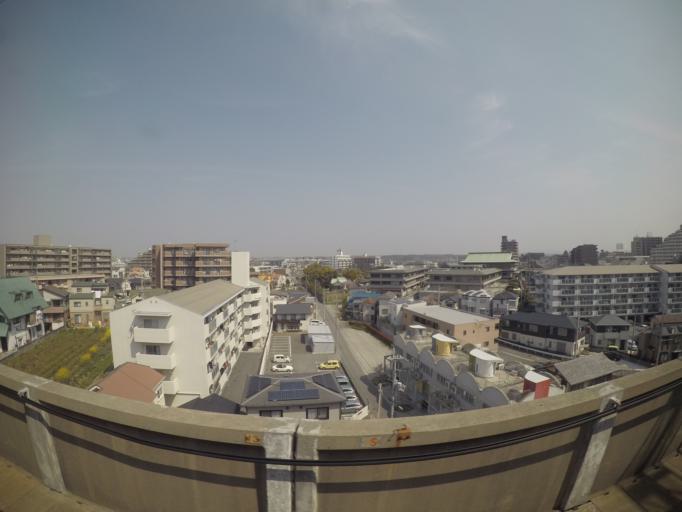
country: JP
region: Hyogo
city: Akashi
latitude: 34.6677
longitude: 134.9544
